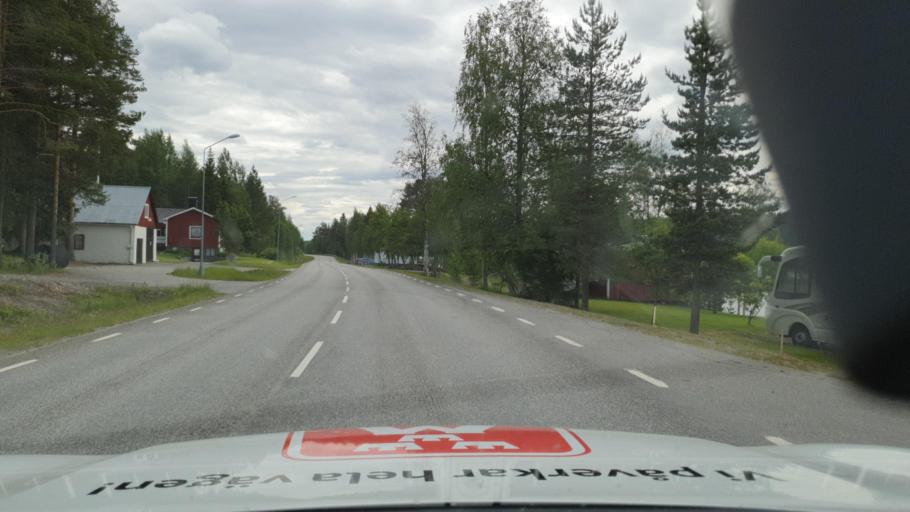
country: SE
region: Vaesterbotten
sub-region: Norsjo Kommun
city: Norsjoe
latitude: 64.9448
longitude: 19.3788
